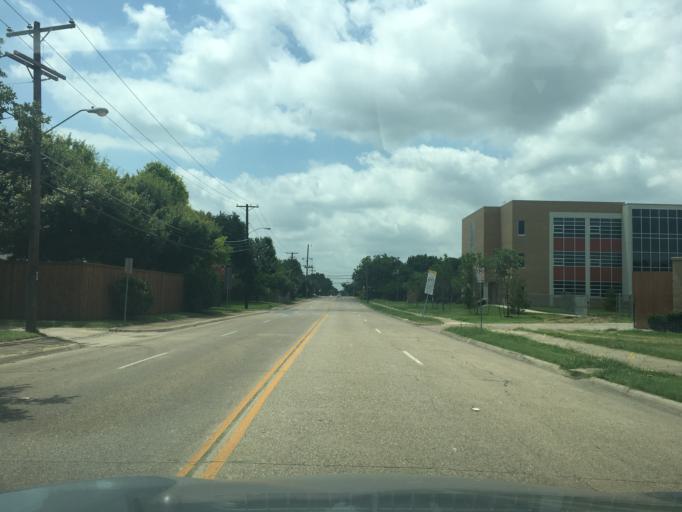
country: US
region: Texas
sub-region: Dallas County
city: Addison
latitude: 32.9168
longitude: -96.8296
